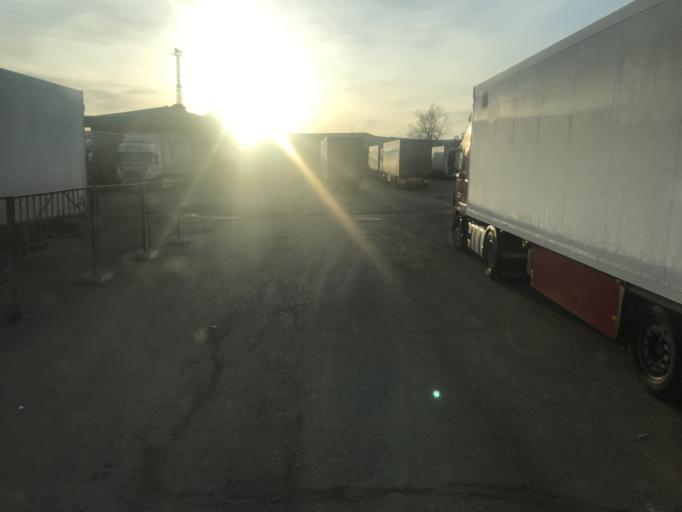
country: AZ
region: Qusar
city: Samur
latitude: 41.6408
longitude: 48.4059
